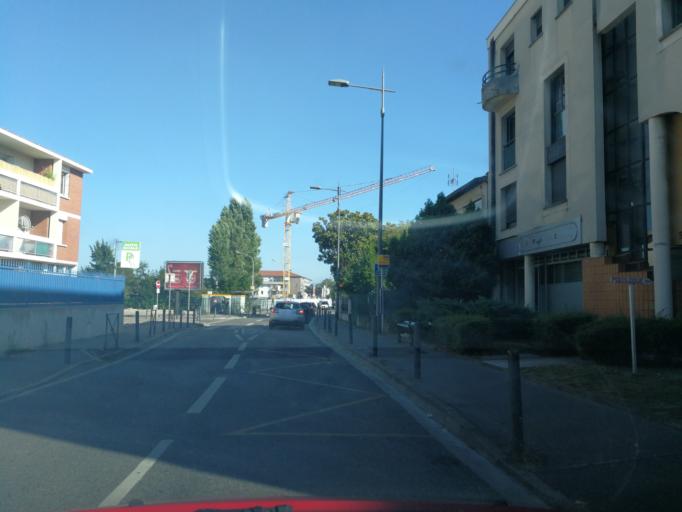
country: FR
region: Midi-Pyrenees
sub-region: Departement de la Haute-Garonne
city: Balma
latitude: 43.6142
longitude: 1.4757
